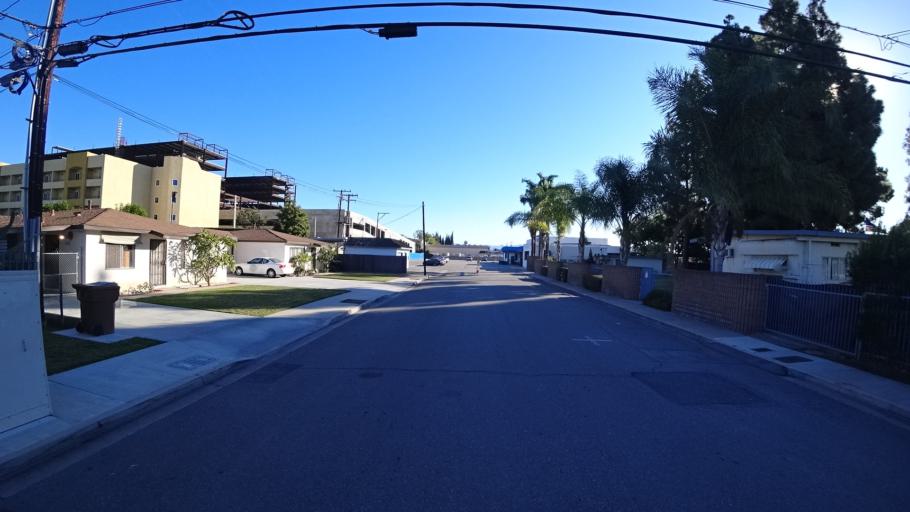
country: US
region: California
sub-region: Orange County
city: Garden Grove
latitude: 33.7725
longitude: -117.9584
